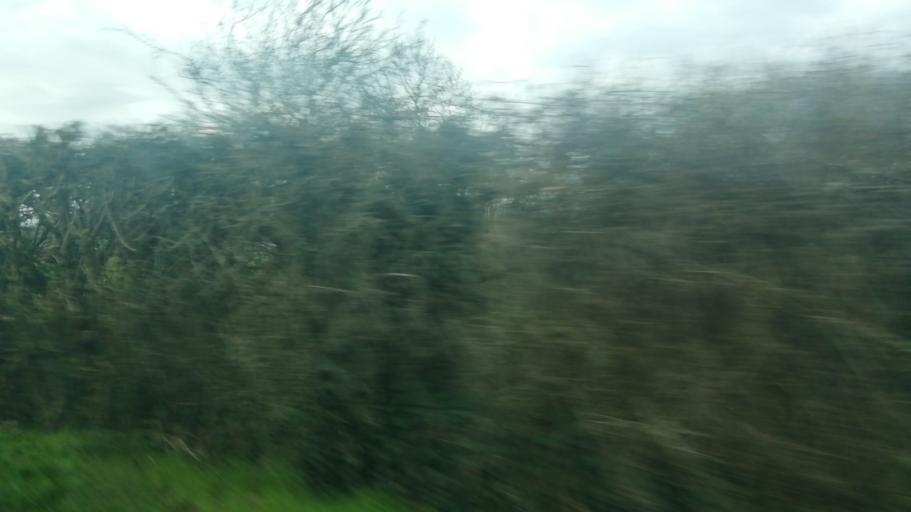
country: IE
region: Leinster
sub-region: Kildare
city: Maynooth
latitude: 53.3554
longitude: -6.6271
